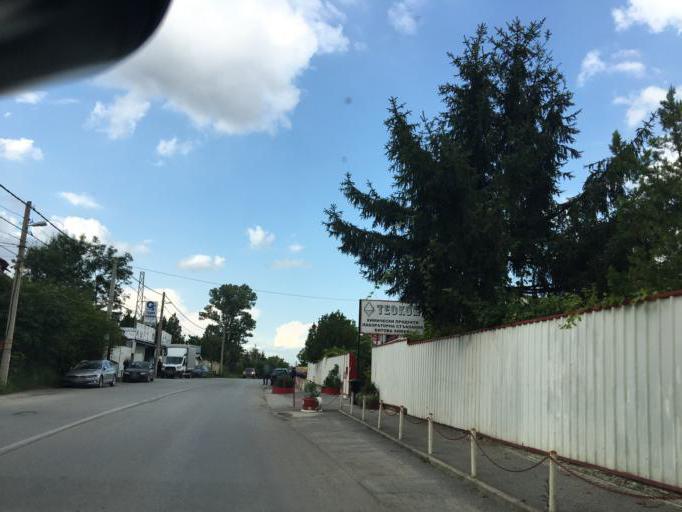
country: BG
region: Sofia-Capital
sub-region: Stolichna Obshtina
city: Sofia
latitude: 42.6407
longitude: 23.3531
